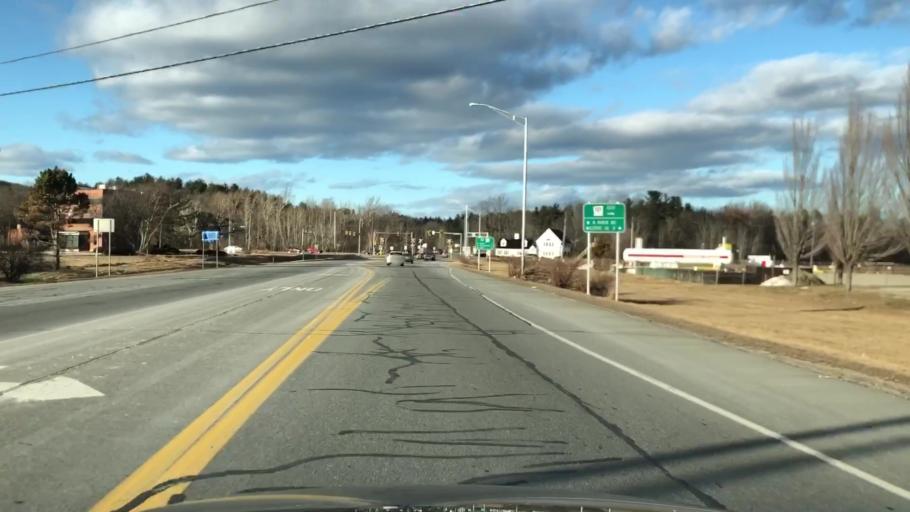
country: US
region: New Hampshire
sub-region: Hillsborough County
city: Wilton
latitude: 42.8402
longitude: -71.7028
